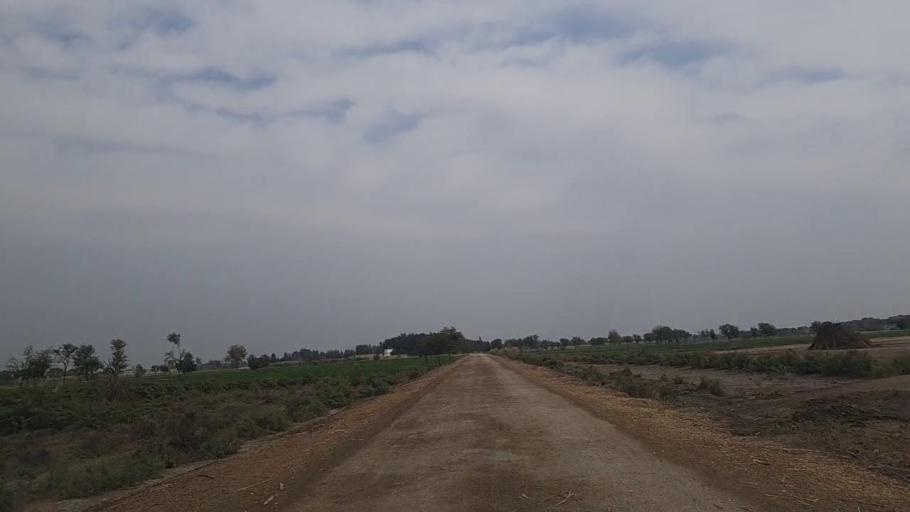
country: PK
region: Sindh
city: Daur
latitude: 26.4192
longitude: 68.4526
